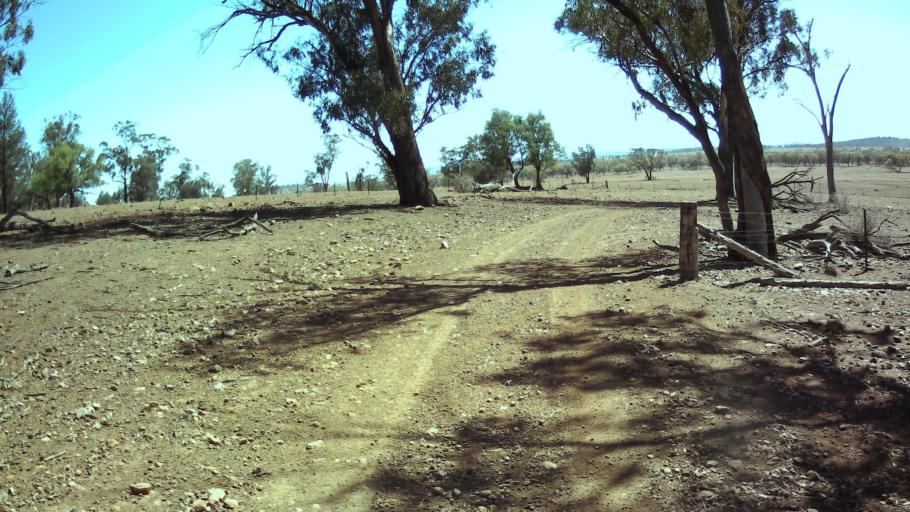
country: AU
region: New South Wales
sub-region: Forbes
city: Forbes
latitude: -33.7322
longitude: 147.6644
